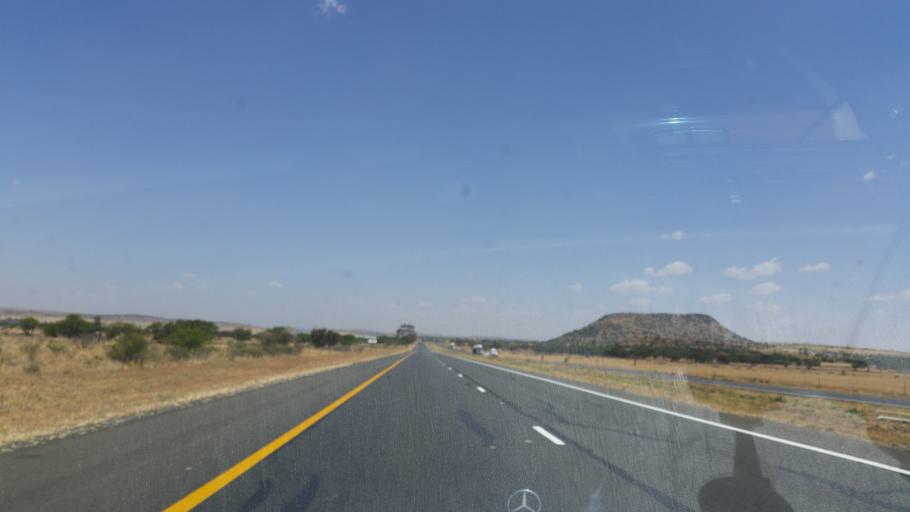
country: ZA
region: Orange Free State
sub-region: Lejweleputswa District Municipality
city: Brandfort
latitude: -28.9456
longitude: 26.4032
